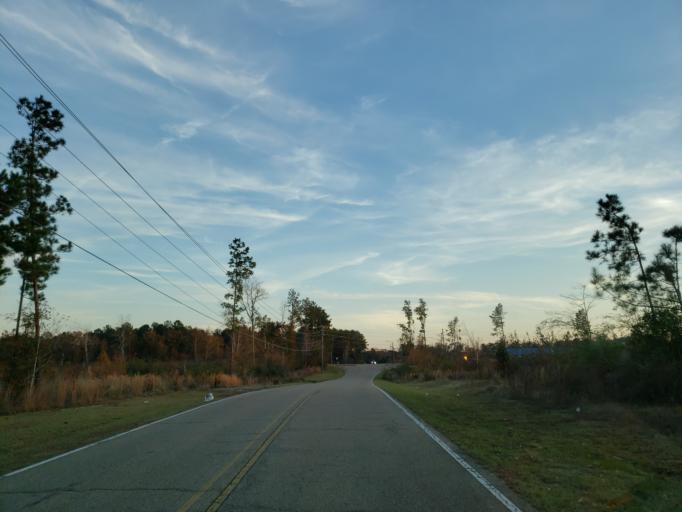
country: US
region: Mississippi
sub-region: Forrest County
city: Hattiesburg
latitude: 31.2926
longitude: -89.3142
